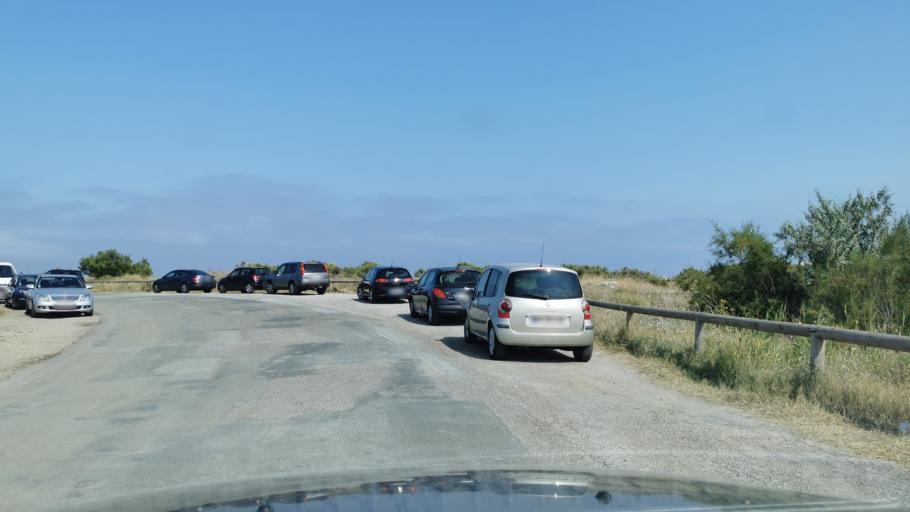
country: FR
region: Languedoc-Roussillon
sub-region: Departement de l'Aude
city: Gruissan
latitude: 43.1134
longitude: 3.1237
